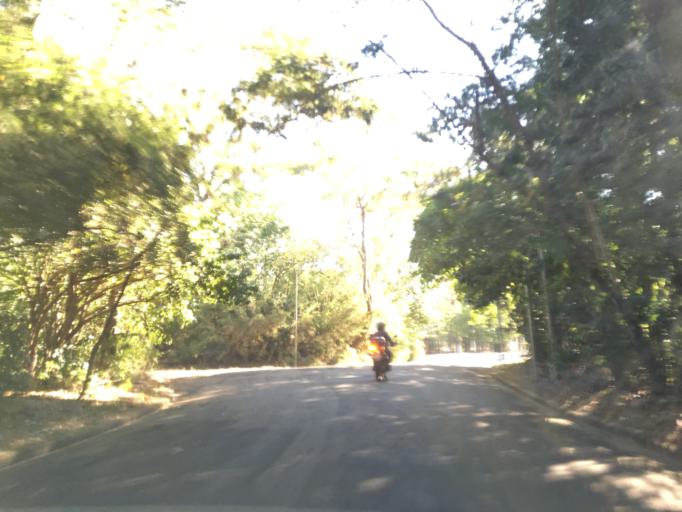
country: BR
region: Sao Paulo
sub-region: Piracicaba
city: Piracicaba
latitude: -22.7118
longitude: -47.6336
